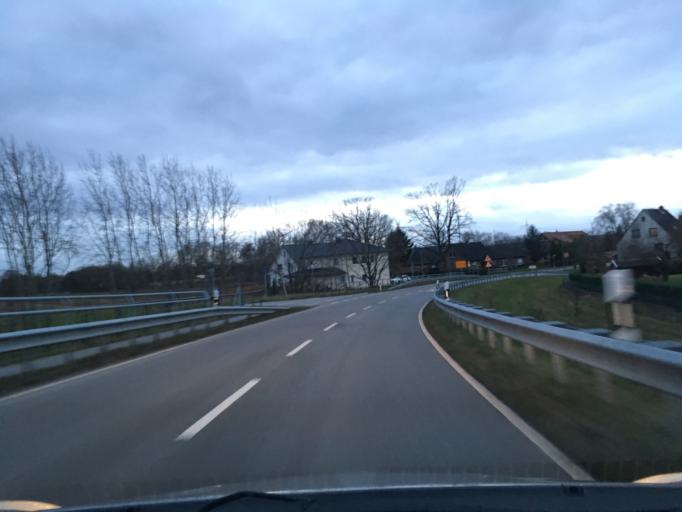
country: DE
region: Lower Saxony
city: Winsen
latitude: 53.3579
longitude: 10.1866
